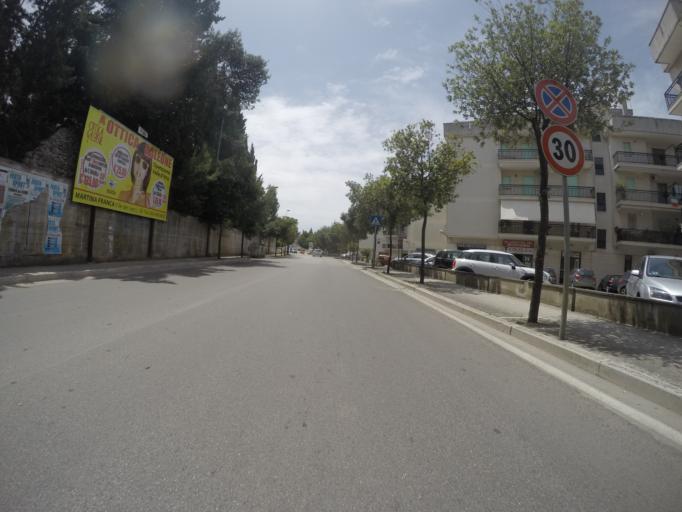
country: IT
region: Apulia
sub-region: Provincia di Taranto
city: Martina Franca
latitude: 40.6981
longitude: 17.3413
